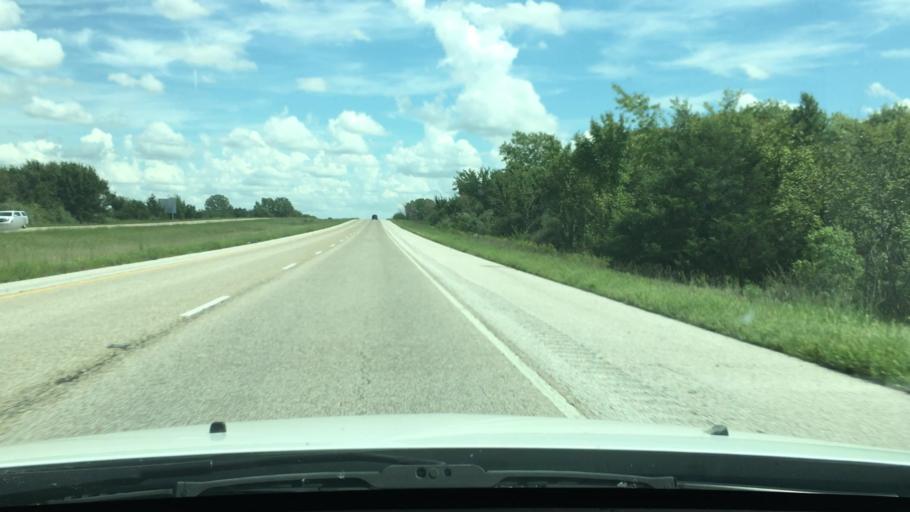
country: US
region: Illinois
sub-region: Scott County
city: Winchester
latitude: 39.6813
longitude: -90.4355
